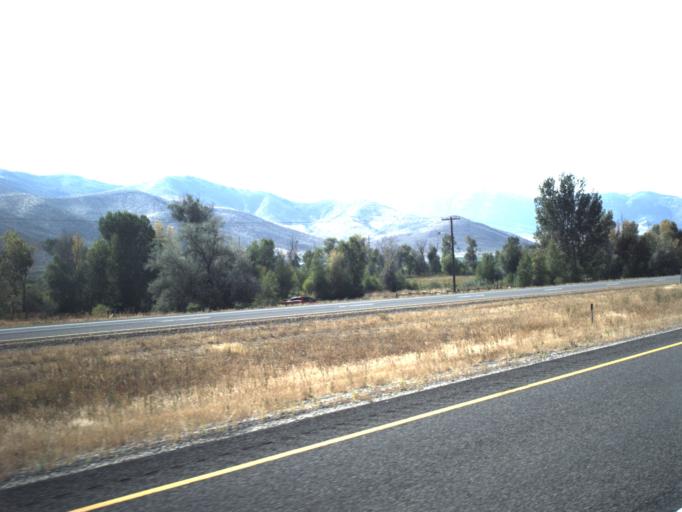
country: US
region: Utah
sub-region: Summit County
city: Coalville
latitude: 41.0027
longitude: -111.4713
